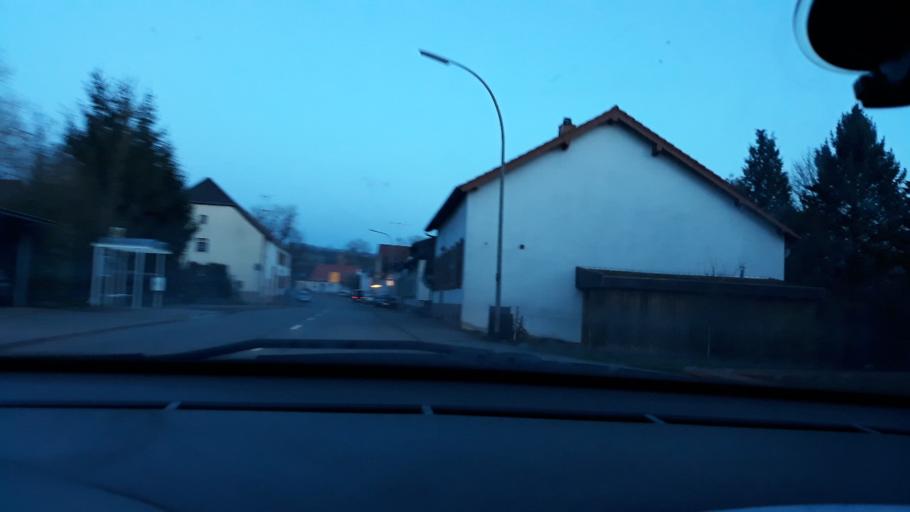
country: FR
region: Lorraine
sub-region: Departement de la Moselle
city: Sarreguemines
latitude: 49.1538
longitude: 7.1106
